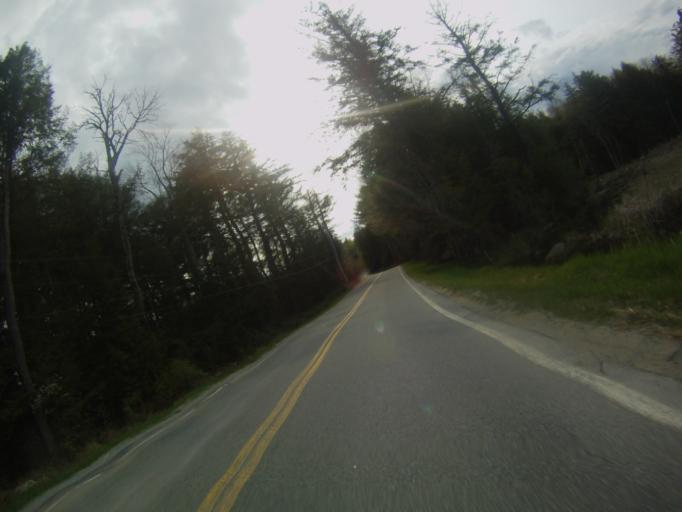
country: US
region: New York
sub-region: Warren County
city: Warrensburg
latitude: 43.8353
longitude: -73.8880
